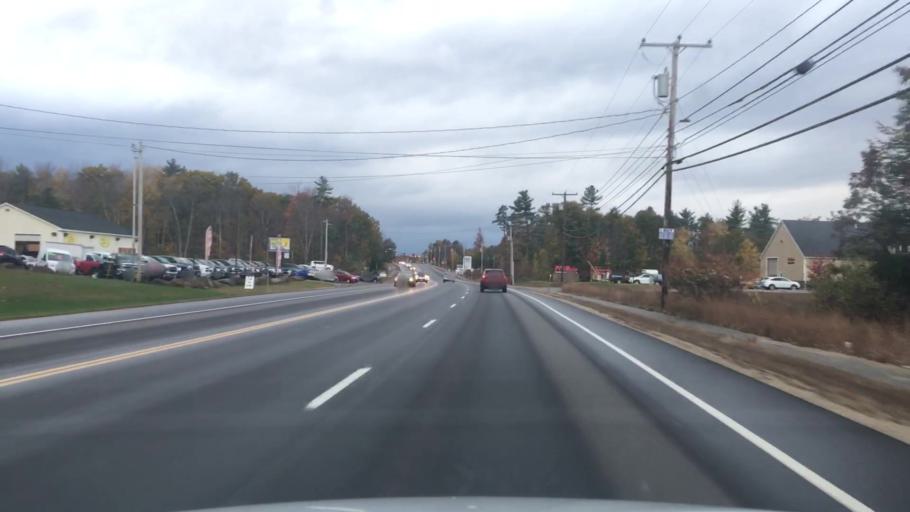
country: US
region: New Hampshire
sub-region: Merrimack County
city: Chichester
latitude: 43.2405
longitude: -71.3969
